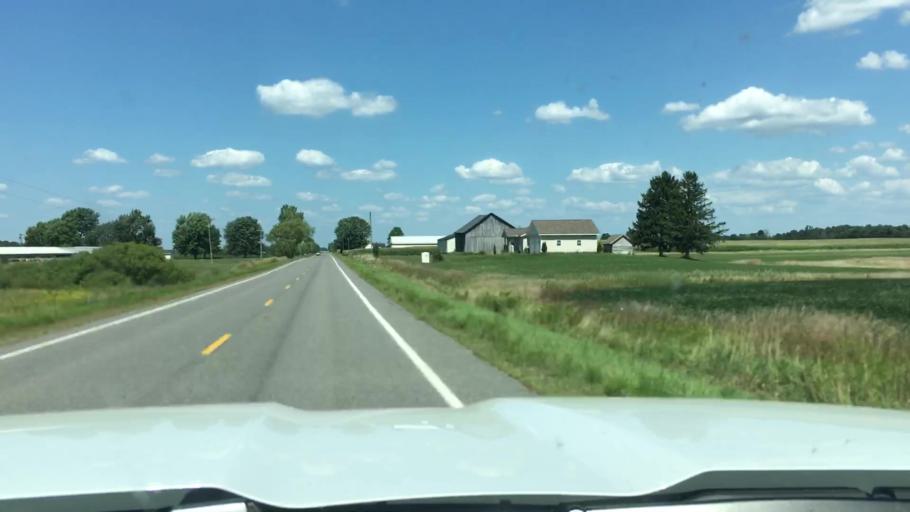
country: US
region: Michigan
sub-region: Muskegon County
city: Ravenna
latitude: 43.1742
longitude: -85.9878
